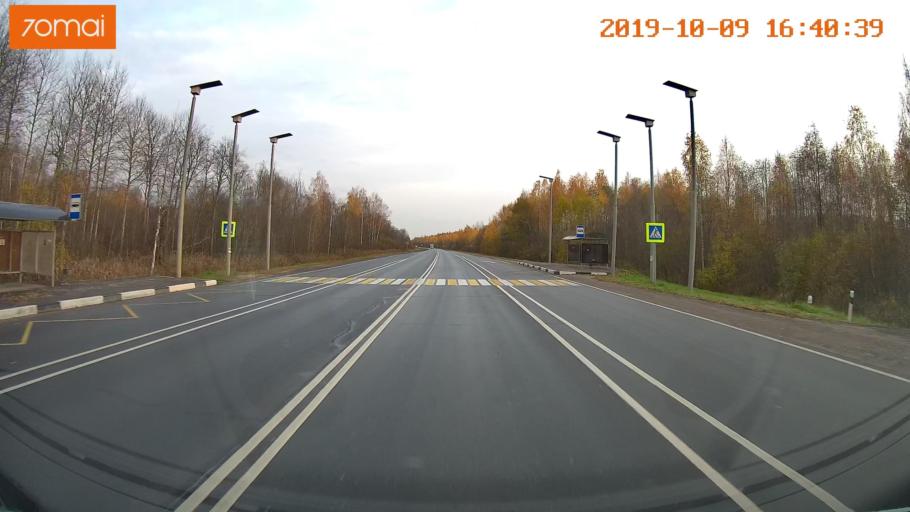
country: RU
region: Kostroma
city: Volgorechensk
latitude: 57.4810
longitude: 41.0643
